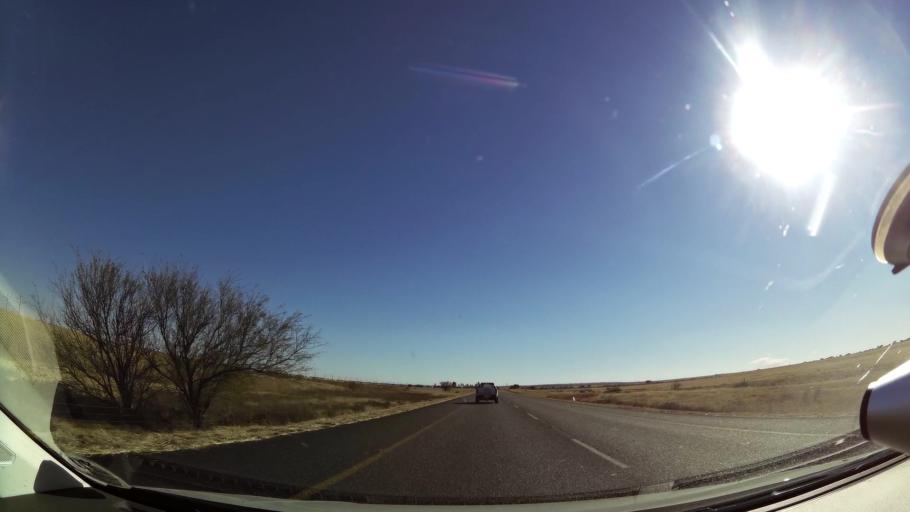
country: ZA
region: Northern Cape
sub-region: Frances Baard District Municipality
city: Kimberley
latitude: -28.6745
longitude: 24.7772
